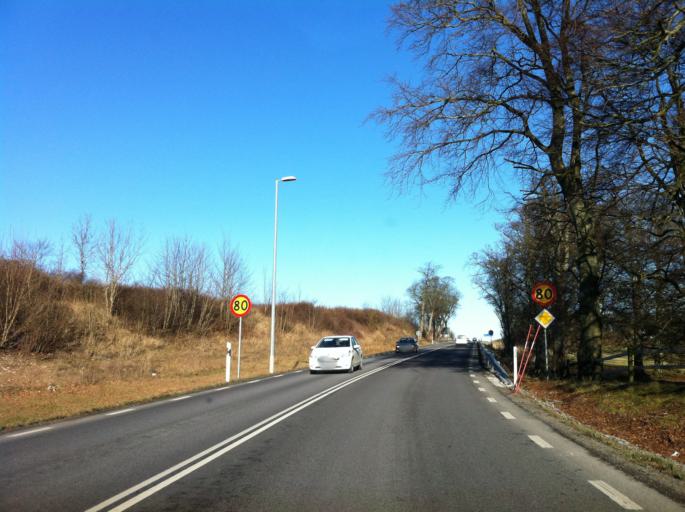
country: SE
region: Skane
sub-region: Svedala Kommun
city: Klagerup
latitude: 55.5927
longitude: 13.2299
